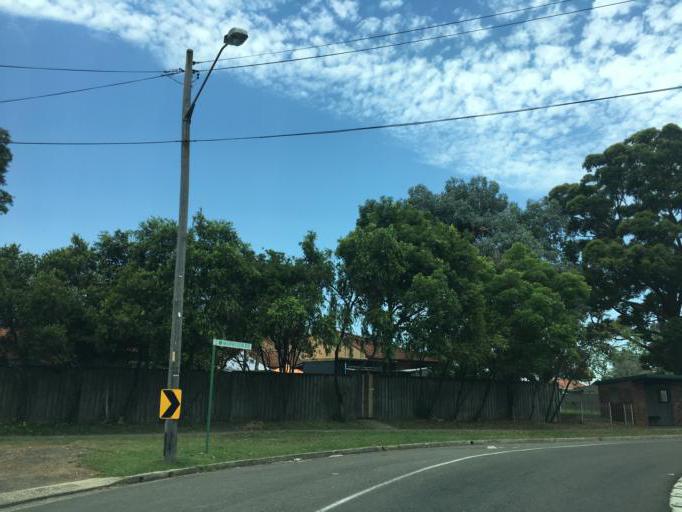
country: AU
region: New South Wales
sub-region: Hunters Hill
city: Gladesville
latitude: -33.8256
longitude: 151.1119
